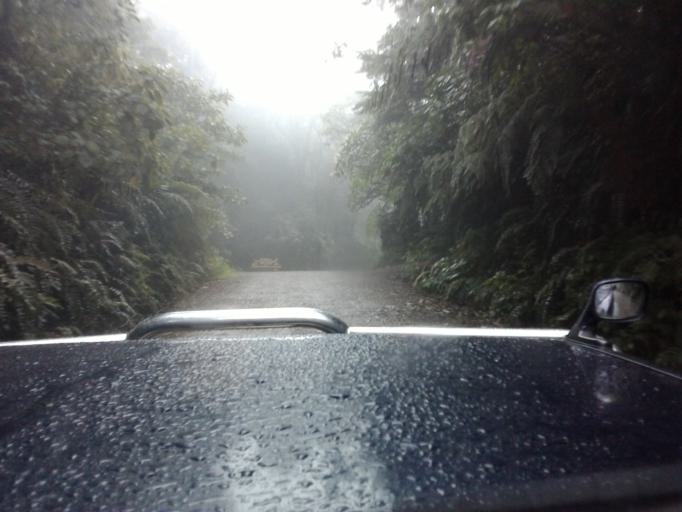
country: CR
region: Guanacaste
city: Juntas
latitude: 10.3429
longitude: -84.7976
